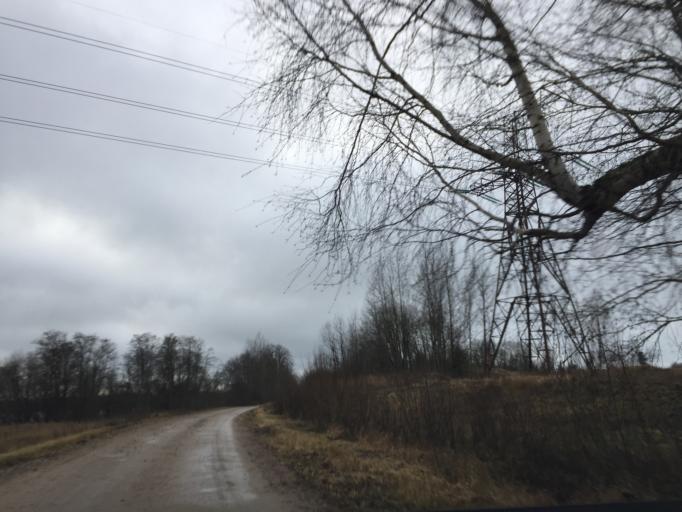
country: LV
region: Broceni
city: Broceni
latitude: 56.6723
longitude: 22.5580
